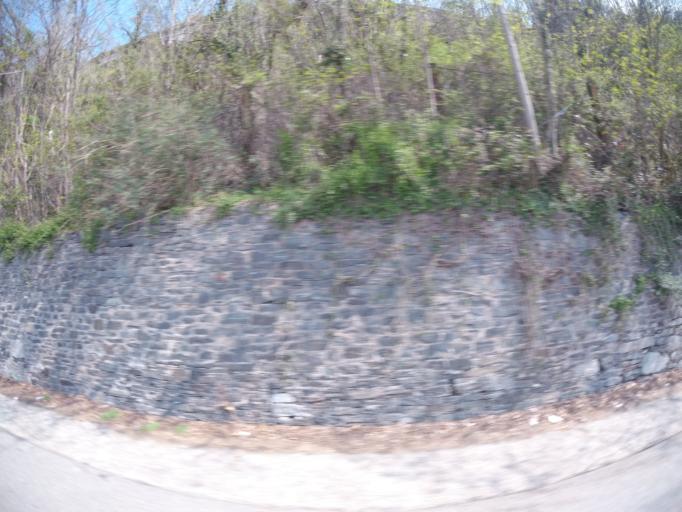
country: IT
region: Piedmont
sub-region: Provincia di Novara
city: Pettenasco
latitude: 45.8086
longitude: 8.4140
